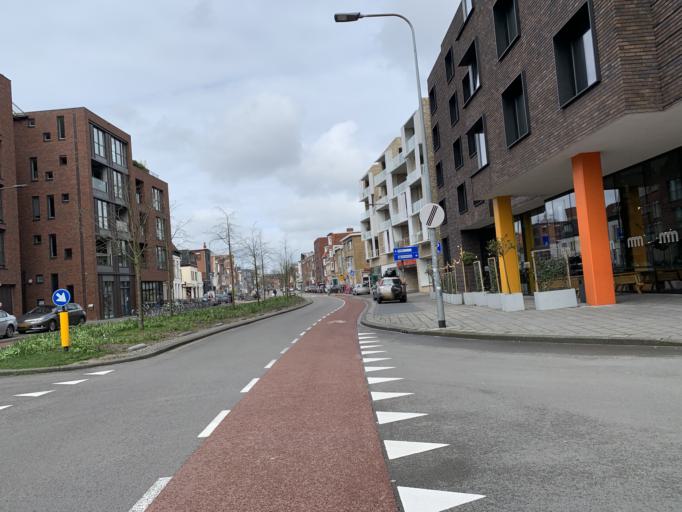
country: NL
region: Groningen
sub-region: Gemeente Groningen
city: Groningen
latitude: 53.2233
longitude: 6.5655
